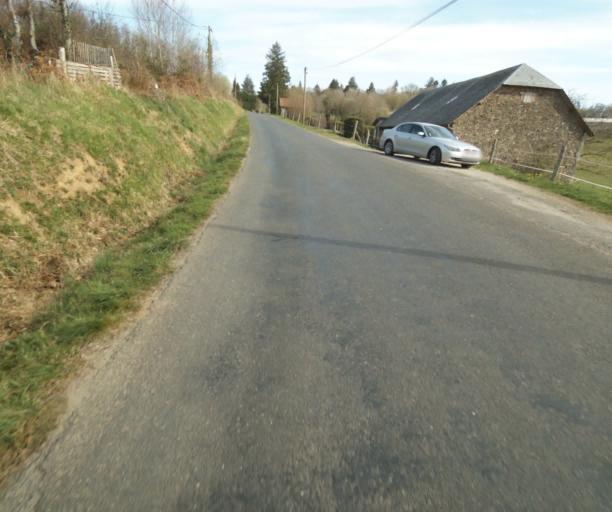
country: FR
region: Limousin
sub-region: Departement de la Correze
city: Naves
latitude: 45.3316
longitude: 1.7496
